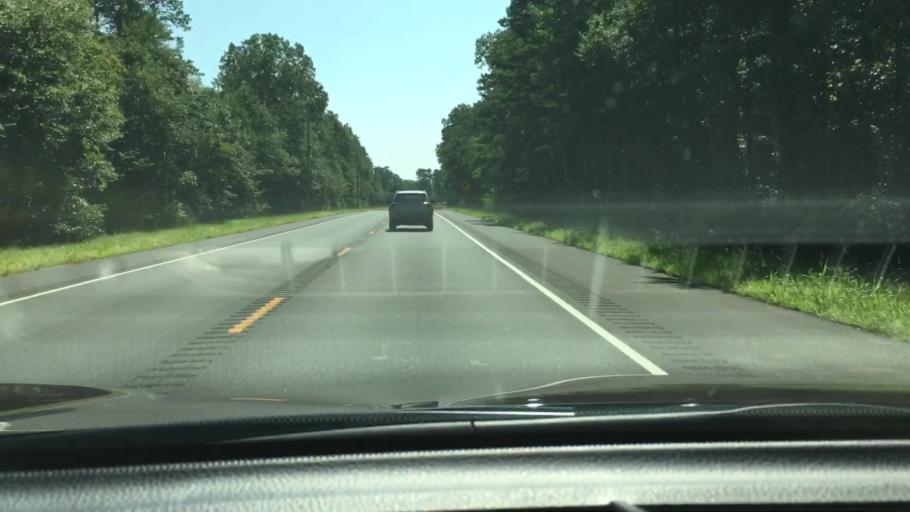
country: US
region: New Jersey
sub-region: Cape May County
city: Woodbine
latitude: 39.3136
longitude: -74.8279
